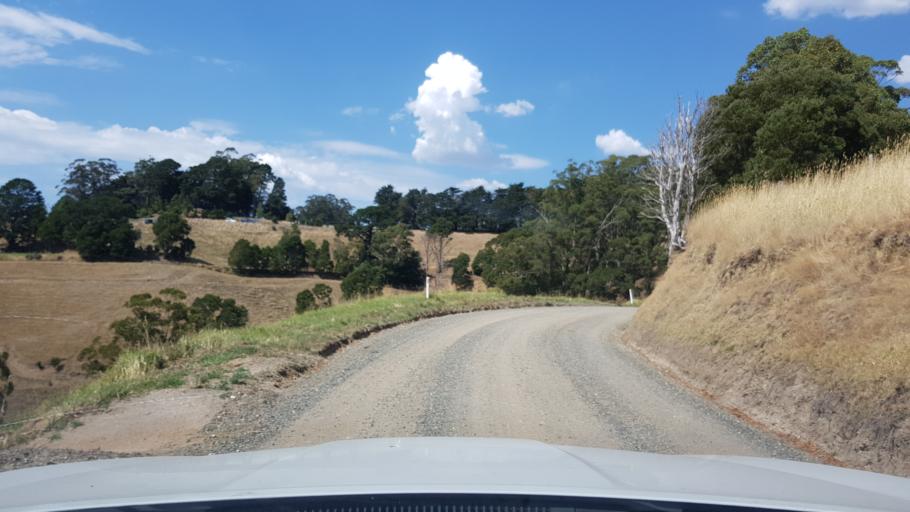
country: AU
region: Victoria
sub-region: Baw Baw
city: Warragul
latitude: -38.2823
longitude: 145.9293
